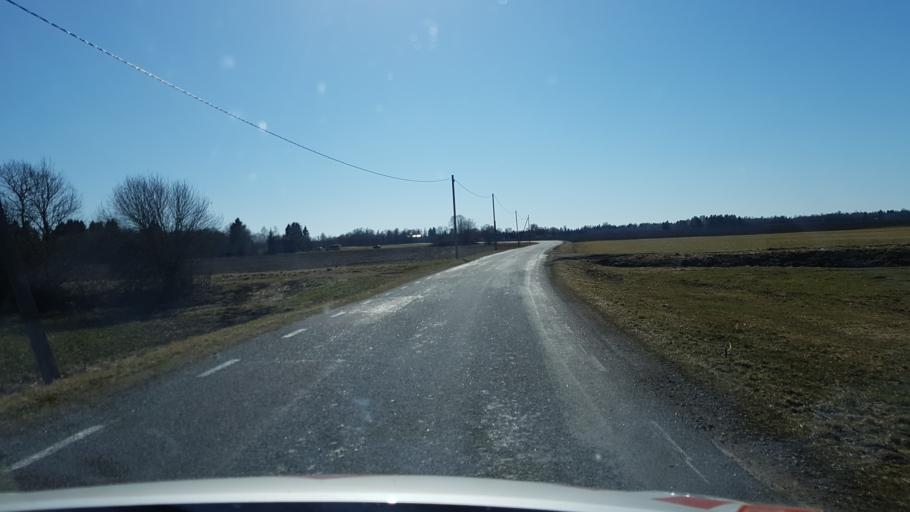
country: EE
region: Laeaene-Virumaa
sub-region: Someru vald
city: Someru
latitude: 59.3819
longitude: 26.4658
